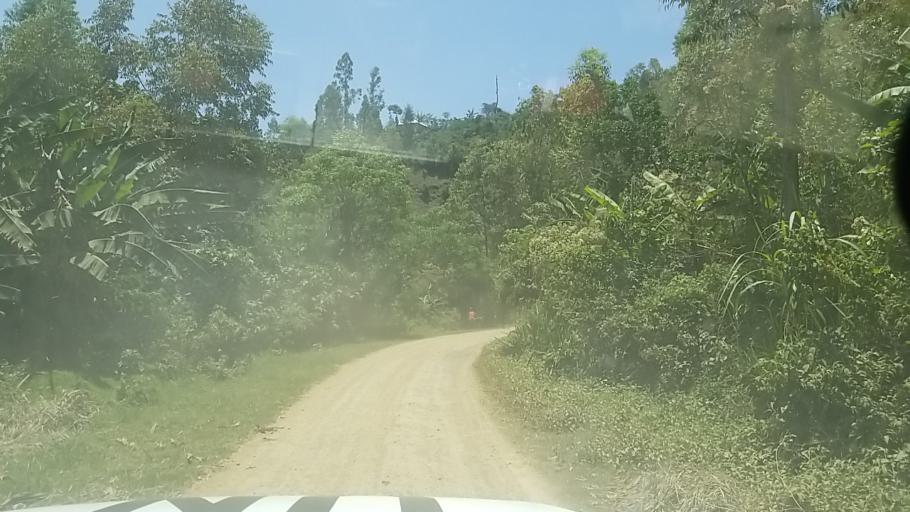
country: CD
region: Nord Kivu
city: Sake
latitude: -1.7758
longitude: 29.0065
